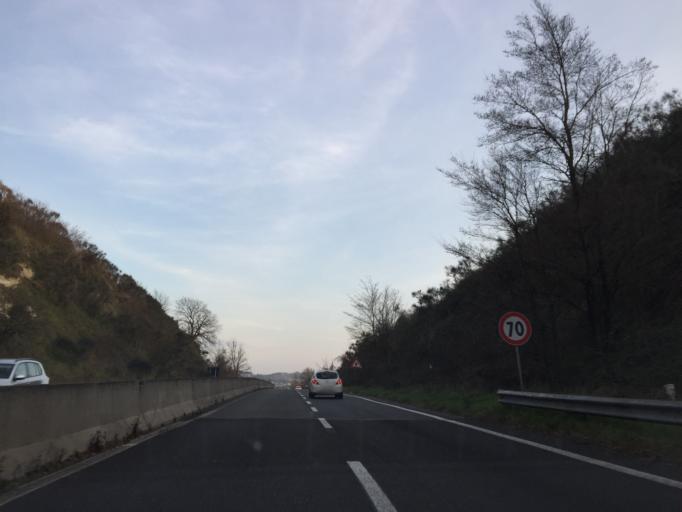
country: IT
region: Latium
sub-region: Citta metropolitana di Roma Capitale
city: Campagnano di Roma
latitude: 42.1363
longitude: 12.3528
